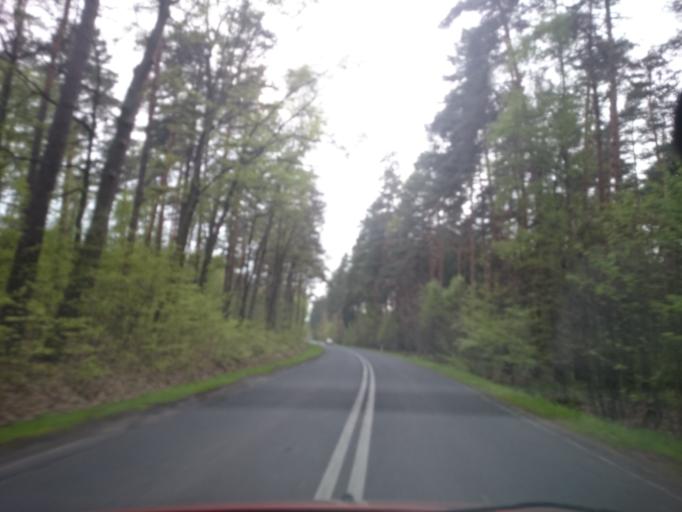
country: PL
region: Opole Voivodeship
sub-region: Powiat opolski
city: Niemodlin
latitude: 50.6264
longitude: 17.5501
